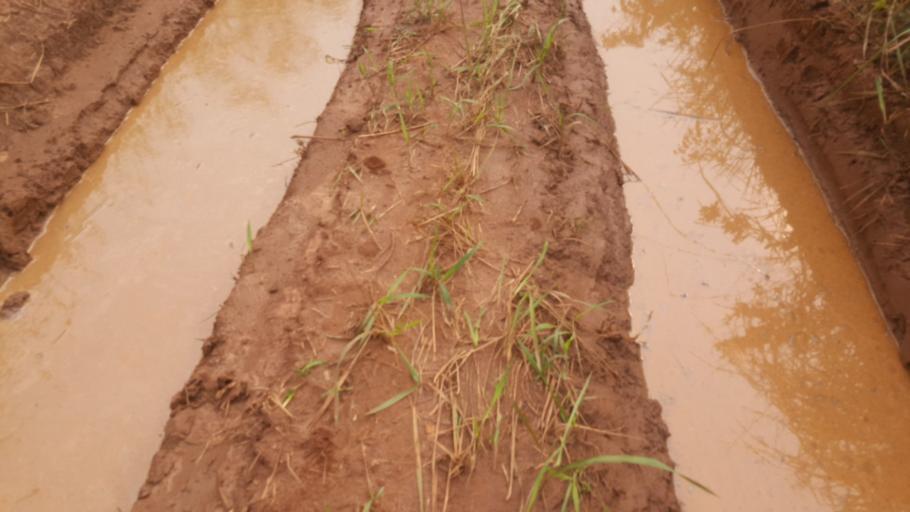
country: CD
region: Bandundu
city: Bandundu
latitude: -3.4667
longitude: 17.7145
